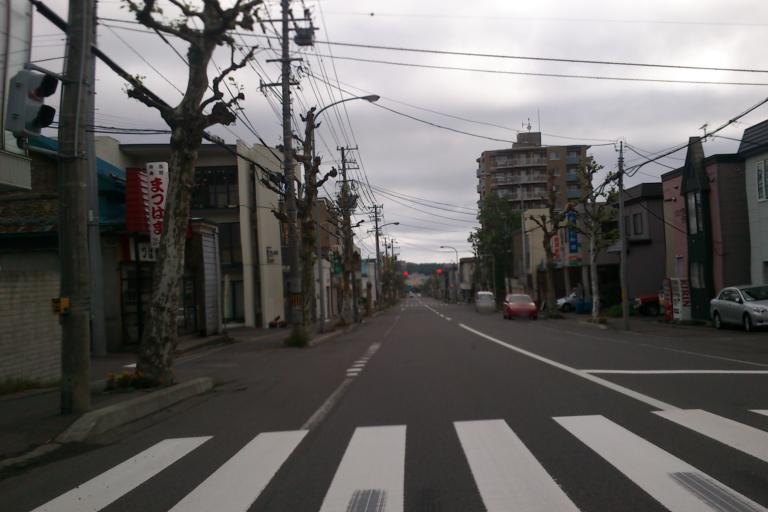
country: JP
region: Hokkaido
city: Otaru
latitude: 43.1883
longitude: 140.9890
